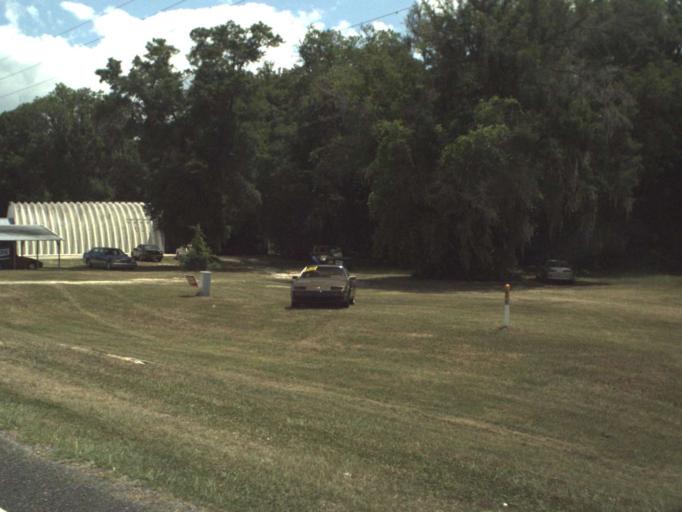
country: US
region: Florida
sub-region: Marion County
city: Ocala
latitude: 29.2256
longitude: -82.1483
